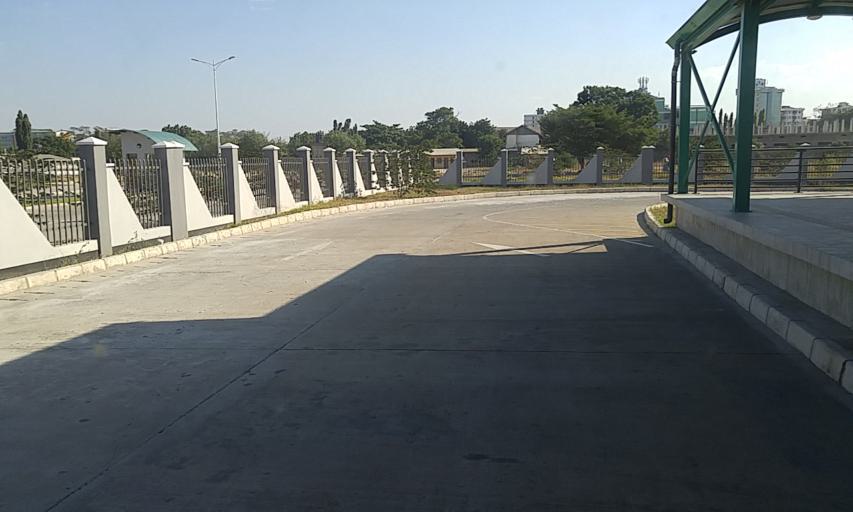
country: TZ
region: Dar es Salaam
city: Dar es Salaam
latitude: -6.8259
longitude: 39.2731
